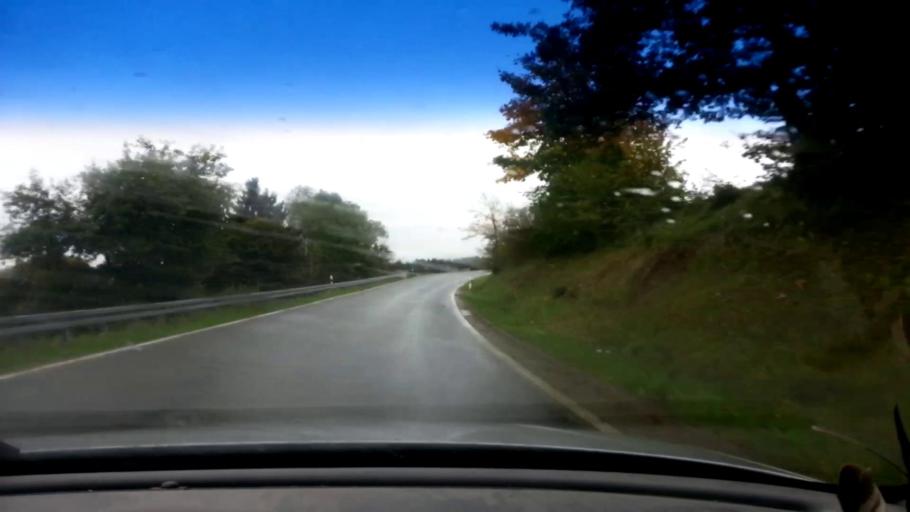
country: DE
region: Bavaria
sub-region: Upper Franconia
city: Poxdorf
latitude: 49.8875
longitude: 11.1104
